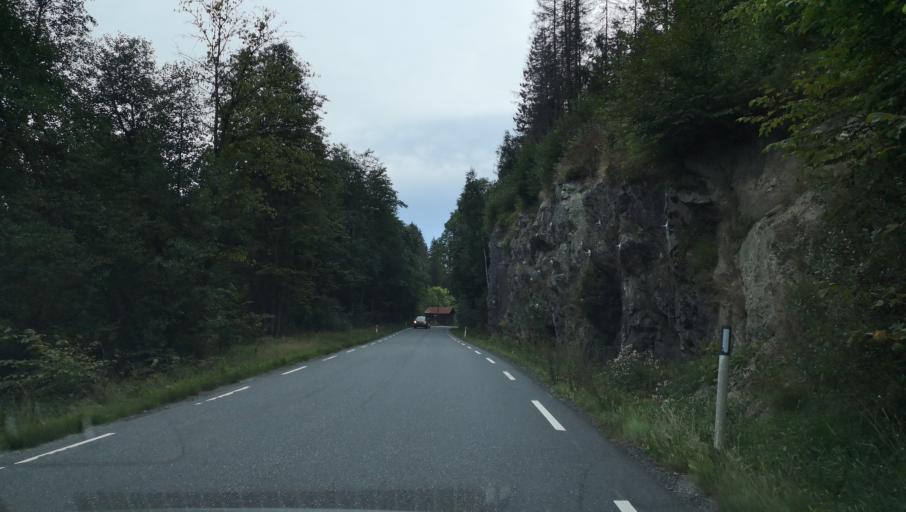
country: NO
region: Ostfold
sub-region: Hobol
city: Tomter
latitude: 59.6730
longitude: 11.0216
